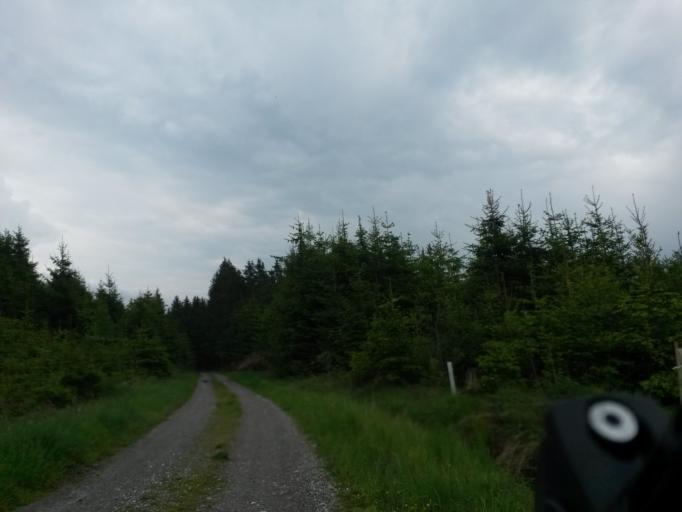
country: DE
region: Baden-Wuerttemberg
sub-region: Tuebingen Region
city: Bad Waldsee
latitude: 47.9225
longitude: 9.8263
